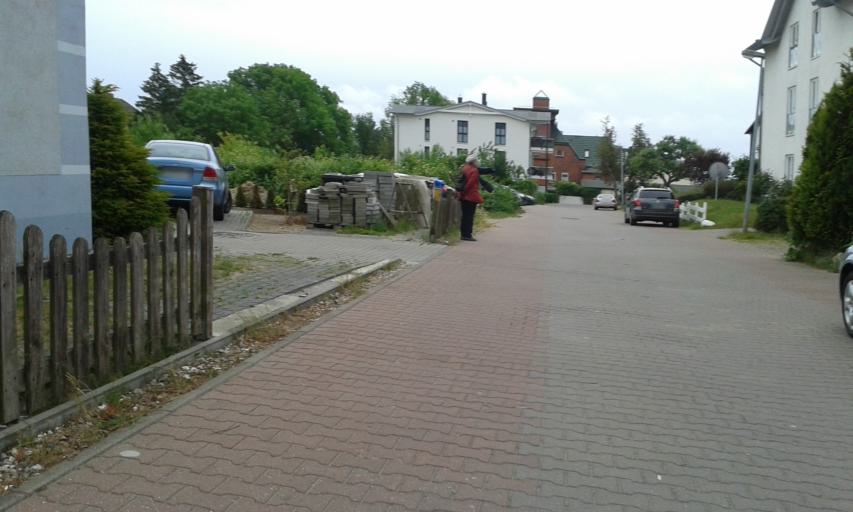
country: DE
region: Mecklenburg-Vorpommern
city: Sassnitz
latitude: 54.5168
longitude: 13.6483
